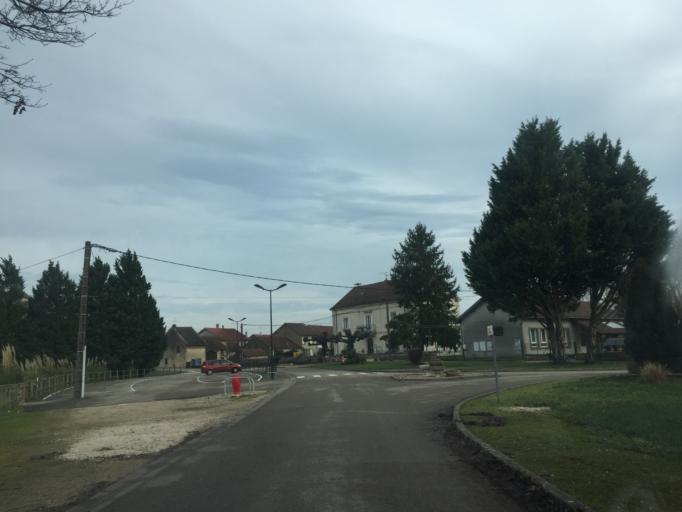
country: FR
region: Franche-Comte
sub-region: Departement du Jura
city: Tavaux
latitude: 47.0179
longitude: 5.4206
